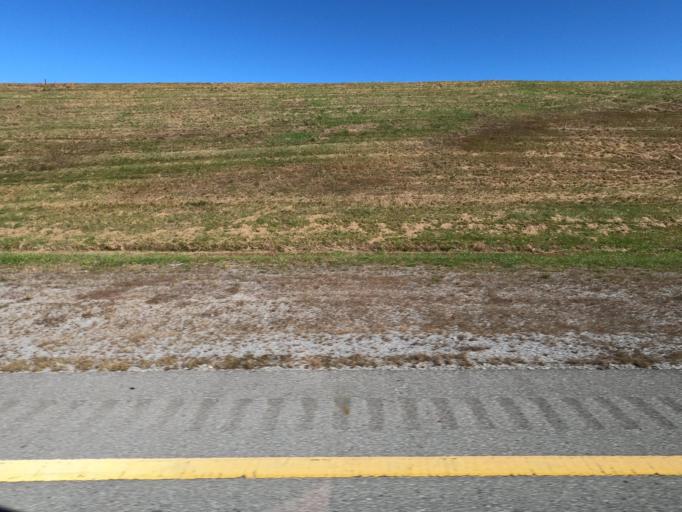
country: US
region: Tennessee
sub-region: Williamson County
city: Fairview
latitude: 35.8911
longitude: -87.1237
